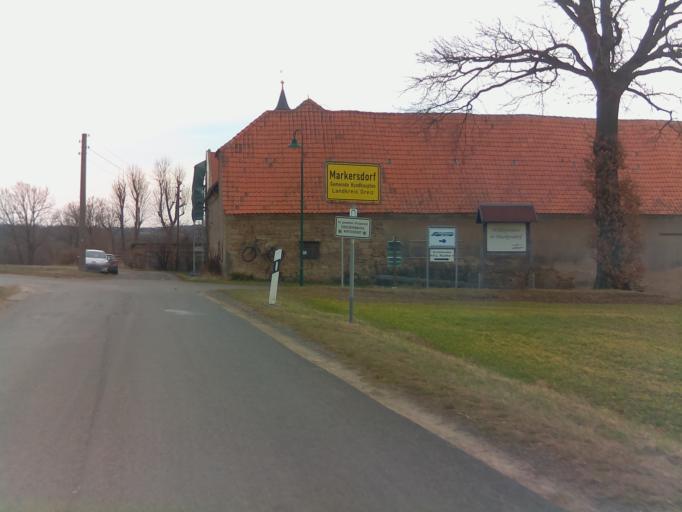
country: DE
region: Thuringia
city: Hundhaupten
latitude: 50.8356
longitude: 11.9963
